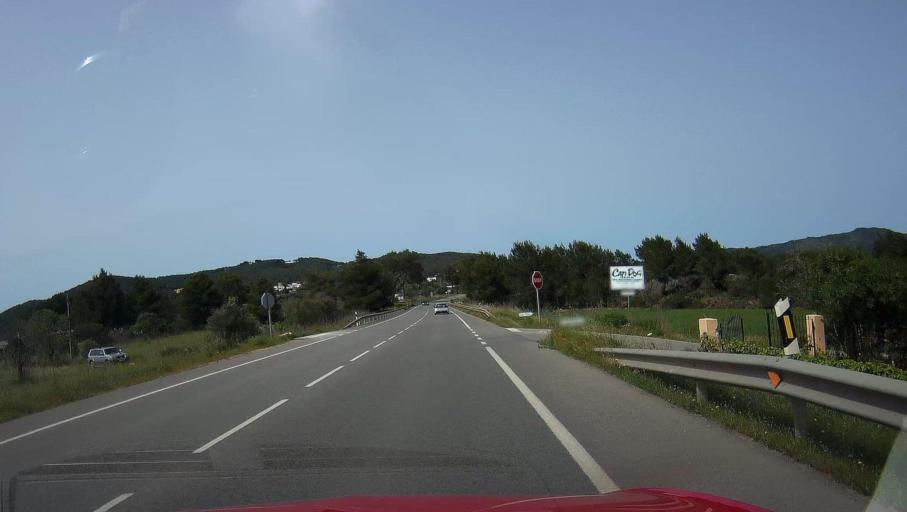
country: ES
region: Balearic Islands
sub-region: Illes Balears
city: Santa Eularia des Riu
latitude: 39.0233
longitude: 1.4872
